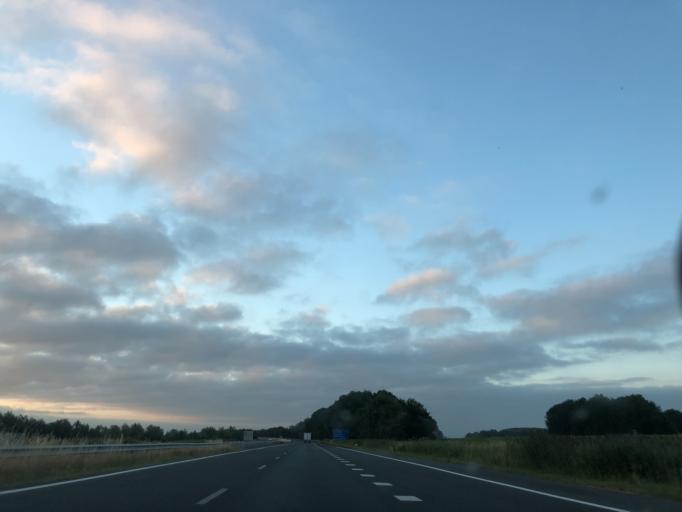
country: NL
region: Groningen
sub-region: Gemeente  Oldambt
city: Winschoten
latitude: 53.1523
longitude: 7.0622
